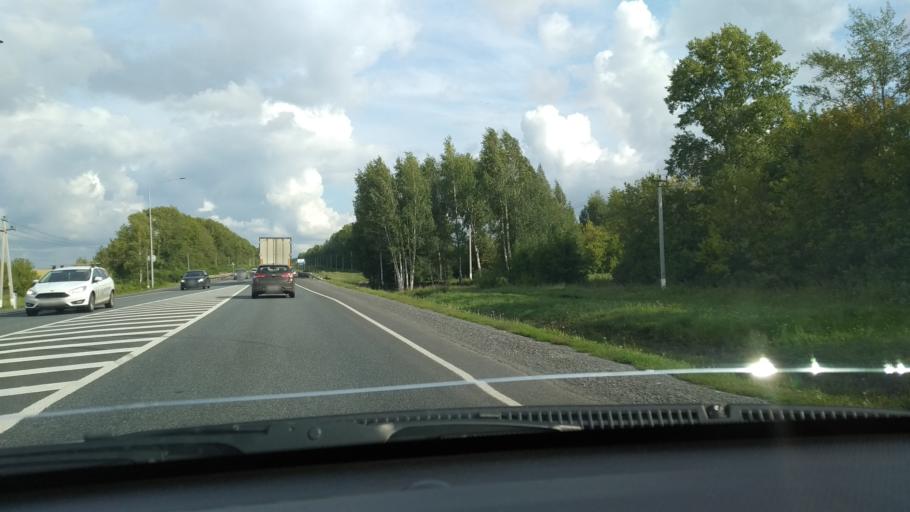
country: RU
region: Tatarstan
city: Stolbishchi
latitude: 55.6526
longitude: 49.3202
